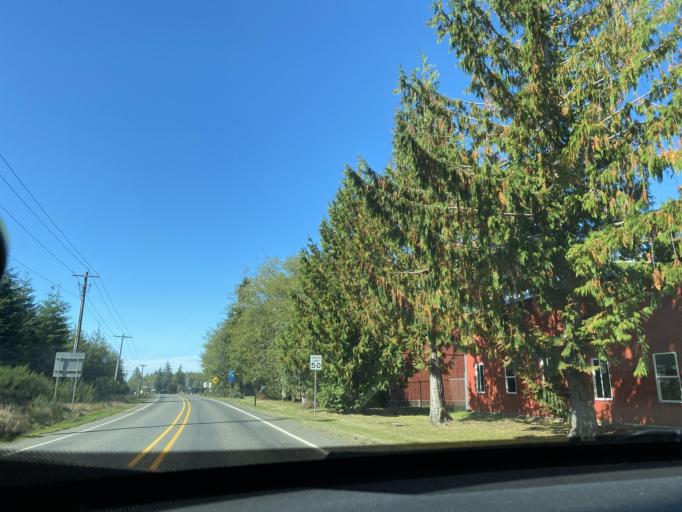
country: US
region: Washington
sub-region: Clallam County
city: Forks
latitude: 47.9674
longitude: -124.4056
